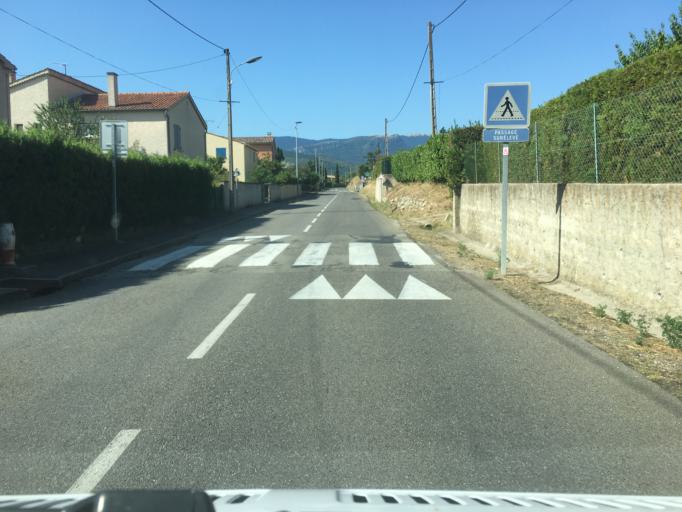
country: FR
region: Provence-Alpes-Cote d'Azur
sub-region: Departement des Alpes-de-Haute-Provence
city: Sisteron
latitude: 44.1848
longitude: 5.9378
